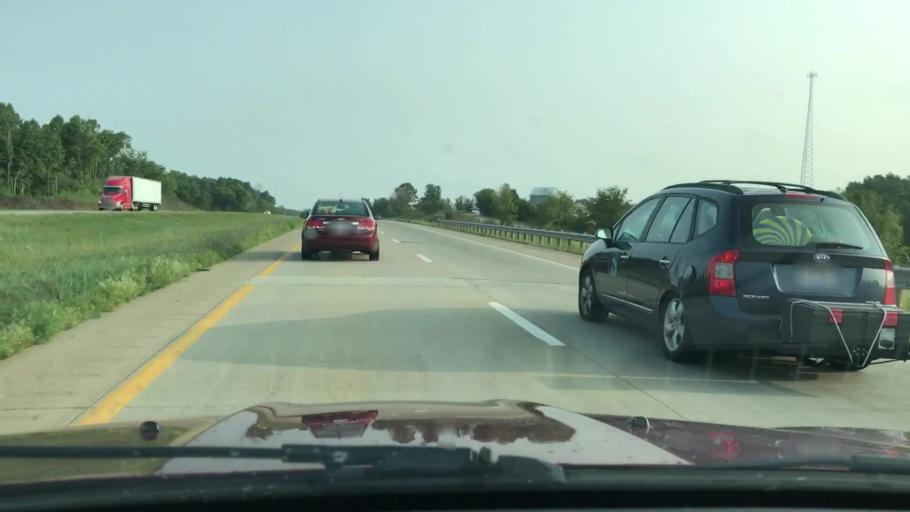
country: US
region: Ohio
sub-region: Washington County
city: Devola
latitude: 39.5559
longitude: -81.4482
